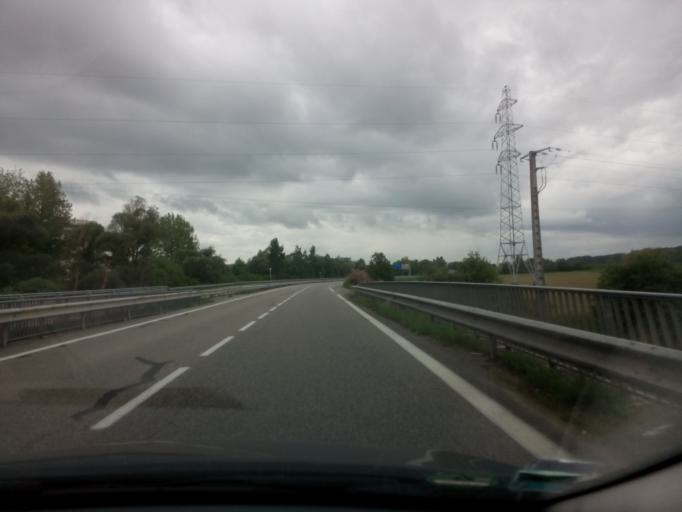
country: FR
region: Alsace
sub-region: Departement du Bas-Rhin
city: Herrlisheim
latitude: 48.7520
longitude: 7.9208
